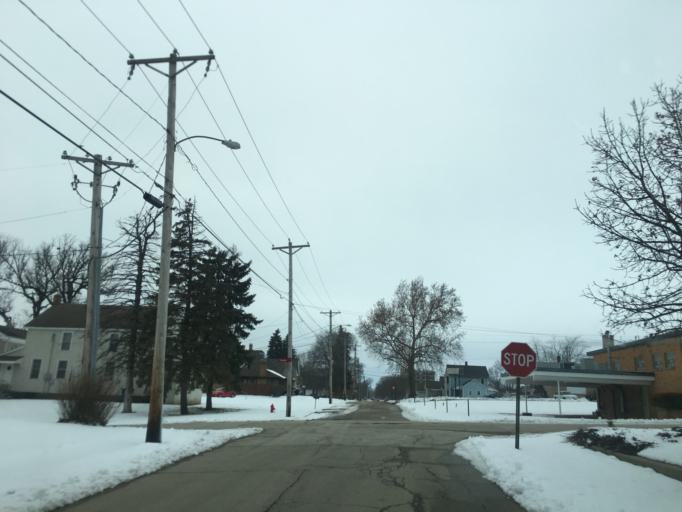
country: US
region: Illinois
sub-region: LaSalle County
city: Peru
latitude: 41.3267
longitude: -89.1289
